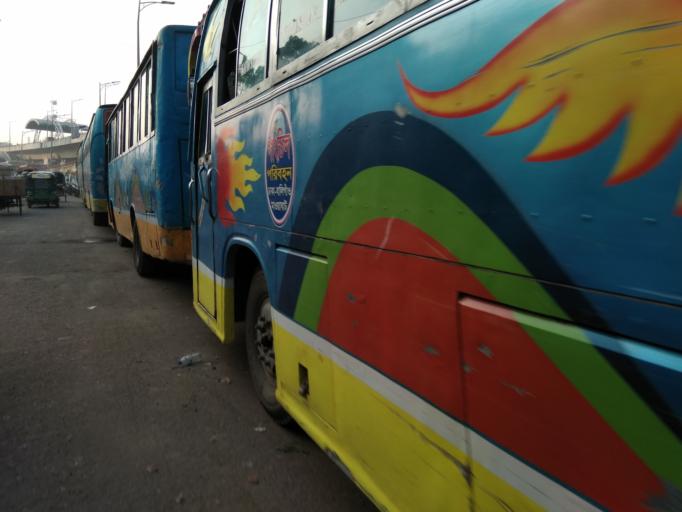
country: BD
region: Dhaka
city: Paltan
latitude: 23.7224
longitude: 90.4149
